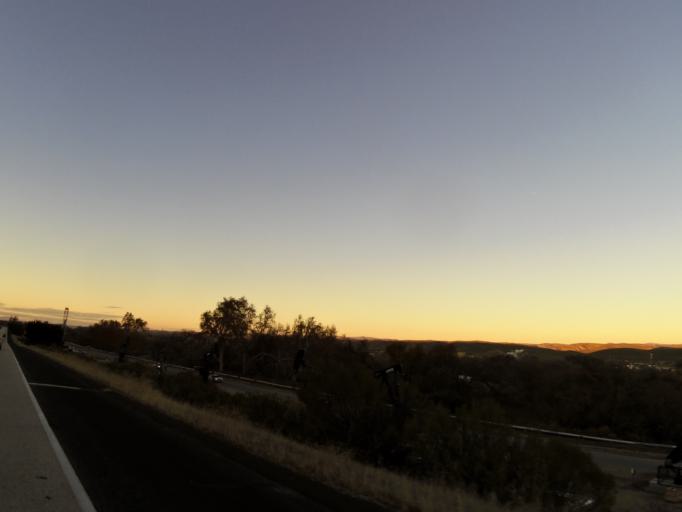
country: US
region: California
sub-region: San Luis Obispo County
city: Lake Nacimiento
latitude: 35.9526
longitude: -120.8793
